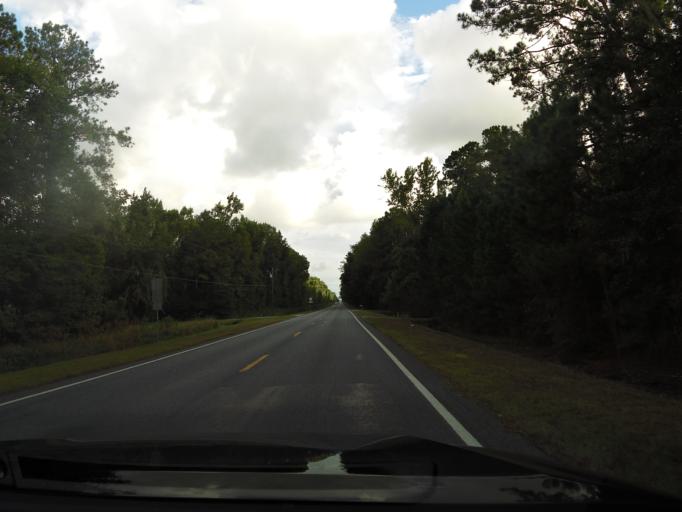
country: US
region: Georgia
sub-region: Liberty County
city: Midway
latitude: 31.6934
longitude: -81.4102
